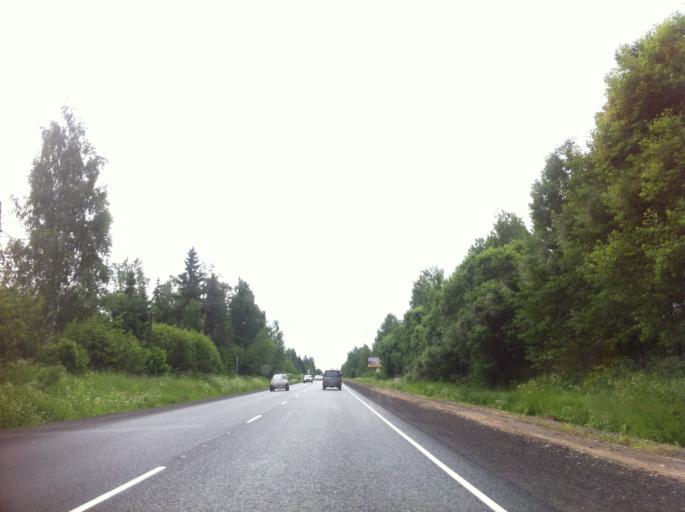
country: RU
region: Leningrad
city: Rozhdestveno
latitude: 59.2395
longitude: 29.9297
